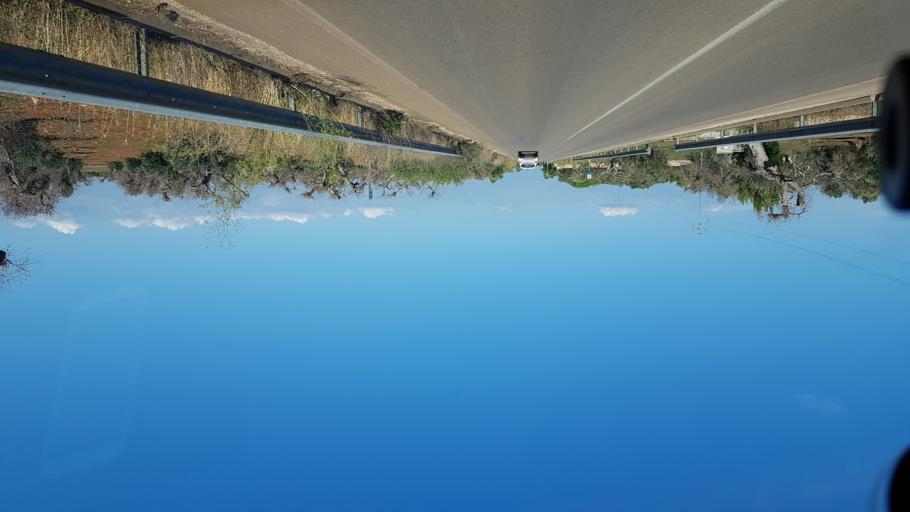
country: IT
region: Apulia
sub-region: Provincia di Lecce
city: Leverano
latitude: 40.2561
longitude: 17.9959
